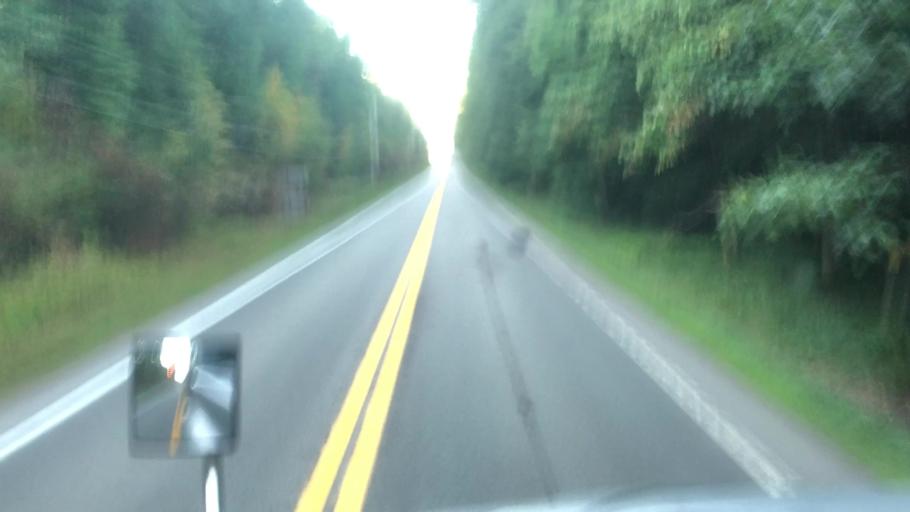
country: US
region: Pennsylvania
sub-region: Crawford County
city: Titusville
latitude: 41.5552
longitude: -79.6111
